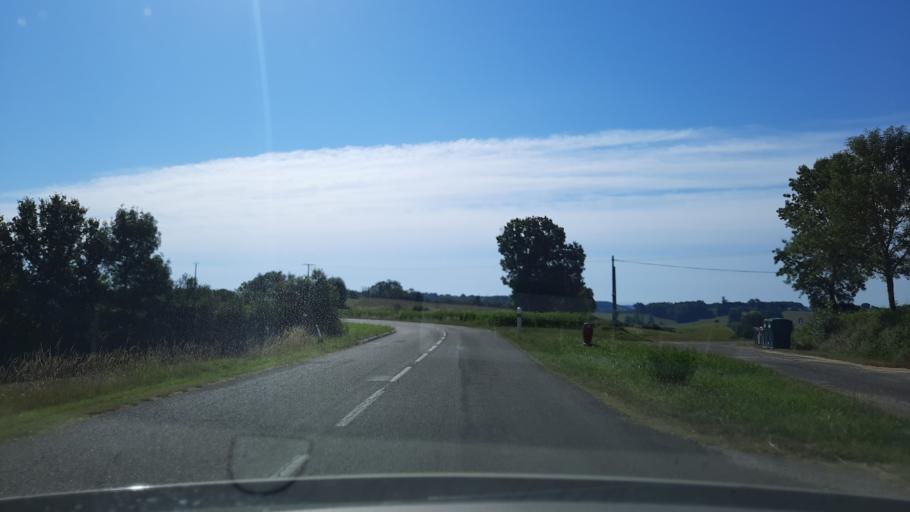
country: FR
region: Midi-Pyrenees
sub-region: Departement du Tarn-et-Garonne
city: Molieres
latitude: 44.1996
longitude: 1.3879
